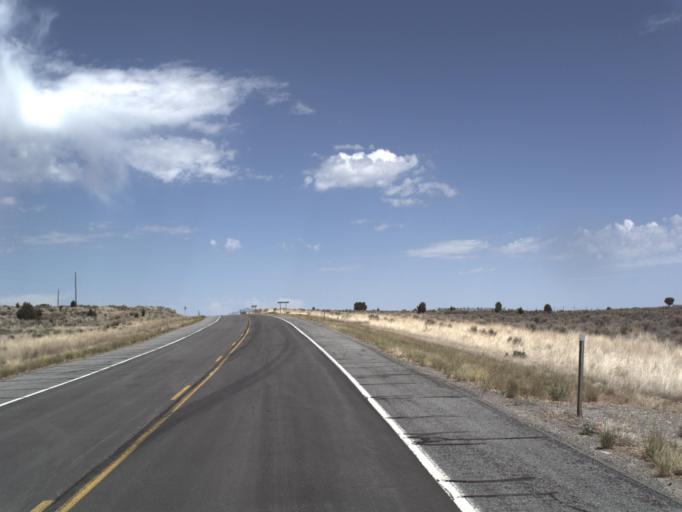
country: US
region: Utah
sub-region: Utah County
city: Eagle Mountain
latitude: 40.0482
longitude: -112.2946
